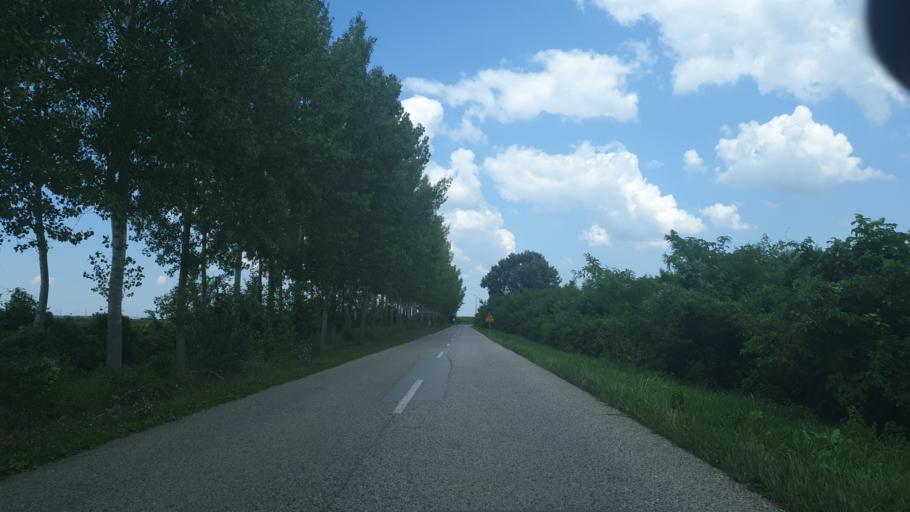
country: RS
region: Autonomna Pokrajina Vojvodina
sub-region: Sremski Okrug
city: Sid
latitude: 45.0417
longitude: 19.2148
